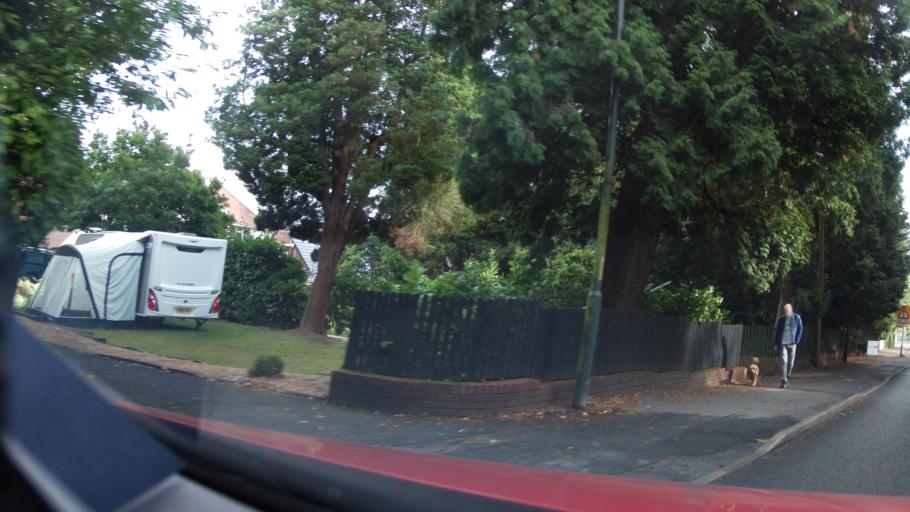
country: GB
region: England
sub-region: Worcestershire
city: Kidderminster
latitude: 52.3813
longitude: -2.2286
